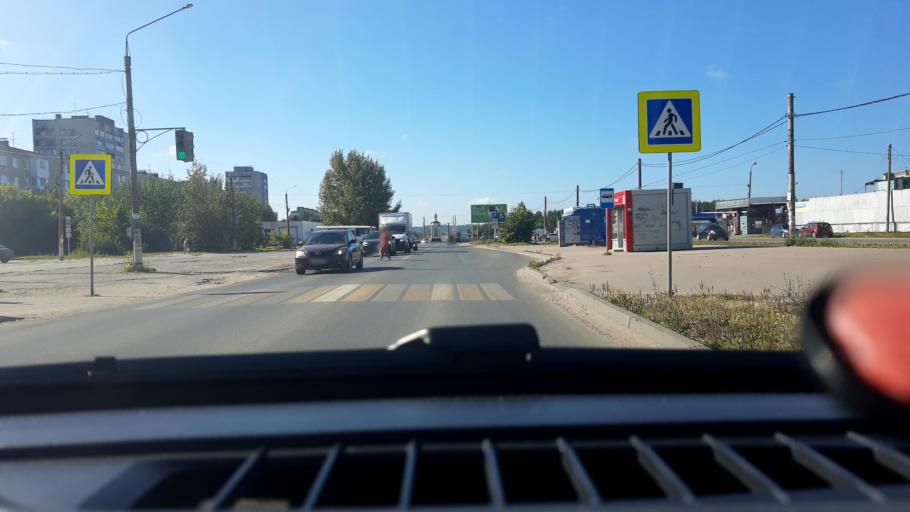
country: RU
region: Nizjnij Novgorod
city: Dzerzhinsk
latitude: 56.2297
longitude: 43.3899
